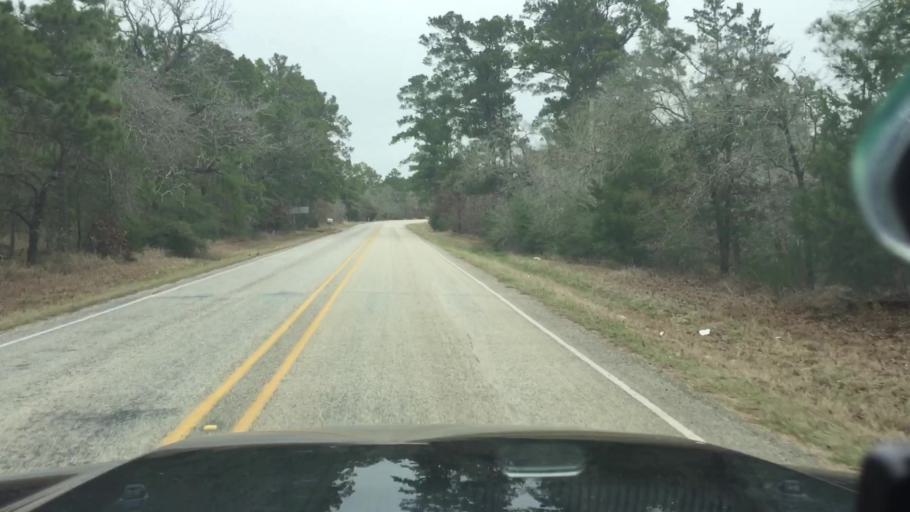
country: US
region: Texas
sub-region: Fayette County
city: La Grange
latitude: 30.0071
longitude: -96.9440
